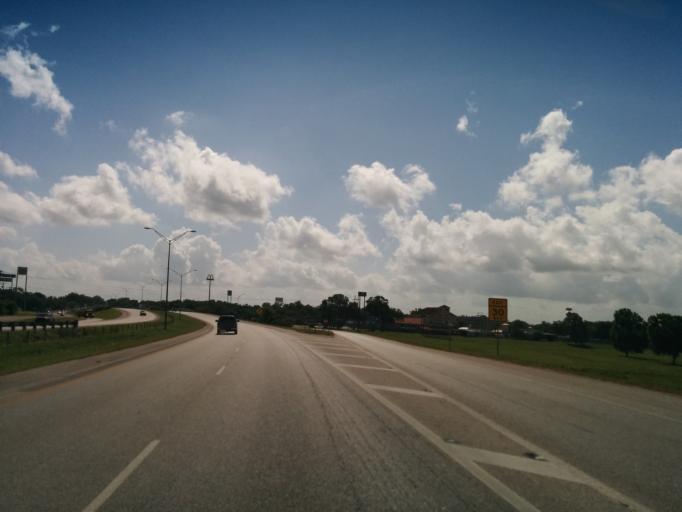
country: US
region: Texas
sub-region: Colorado County
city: Columbus
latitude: 29.6918
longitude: -96.5437
